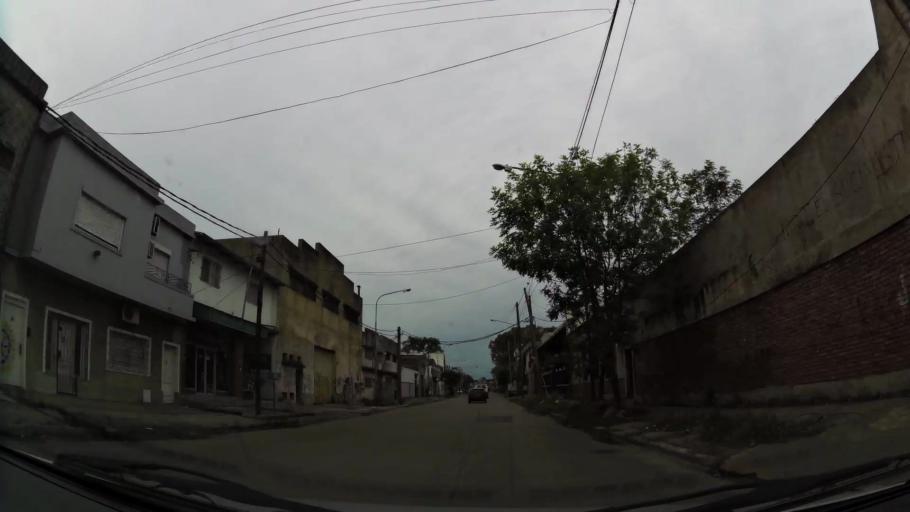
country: AR
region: Buenos Aires
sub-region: Partido de Lanus
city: Lanus
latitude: -34.6991
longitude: -58.3720
